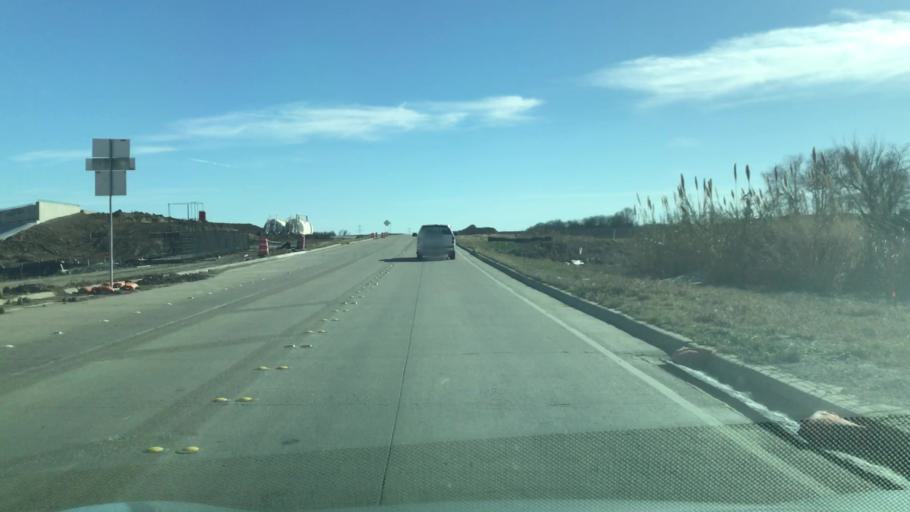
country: US
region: Texas
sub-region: Tarrant County
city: Mansfield
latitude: 32.5449
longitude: -97.0838
